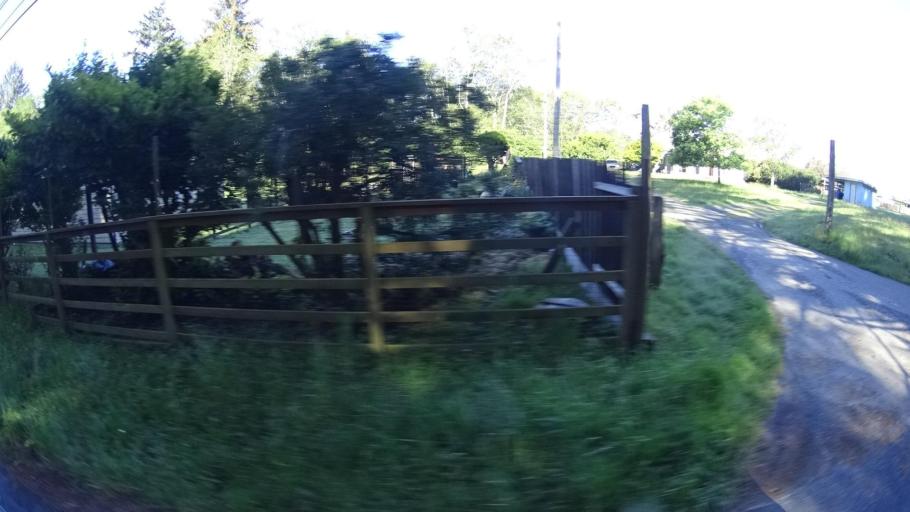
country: US
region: California
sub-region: Humboldt County
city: McKinleyville
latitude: 40.9870
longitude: -124.1005
